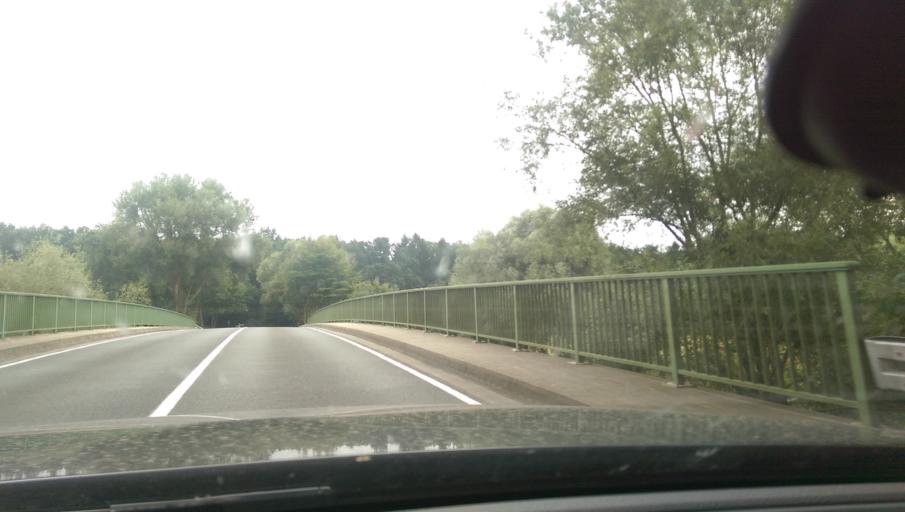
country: DE
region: Lower Saxony
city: Neustadt am Rubenberge
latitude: 52.5560
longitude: 9.5050
